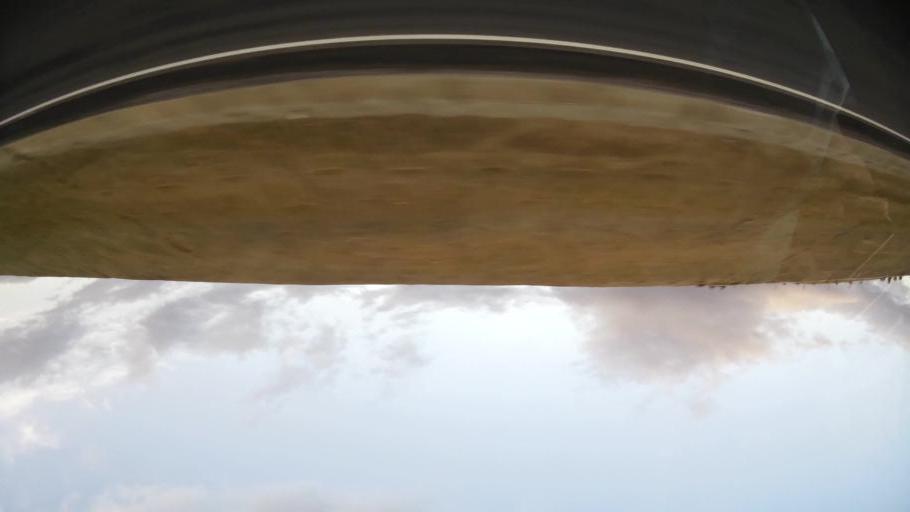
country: MA
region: Oriental
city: Taourirt
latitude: 34.5773
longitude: -2.8115
